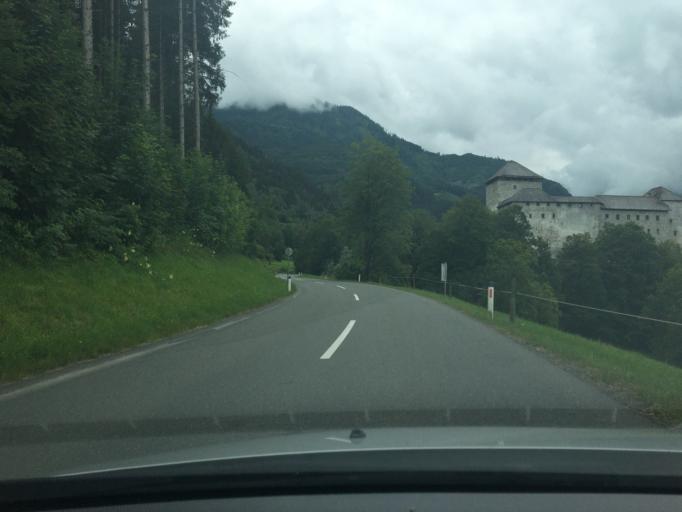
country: AT
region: Salzburg
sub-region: Politischer Bezirk Zell am See
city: Kaprun
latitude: 47.2759
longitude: 12.7726
